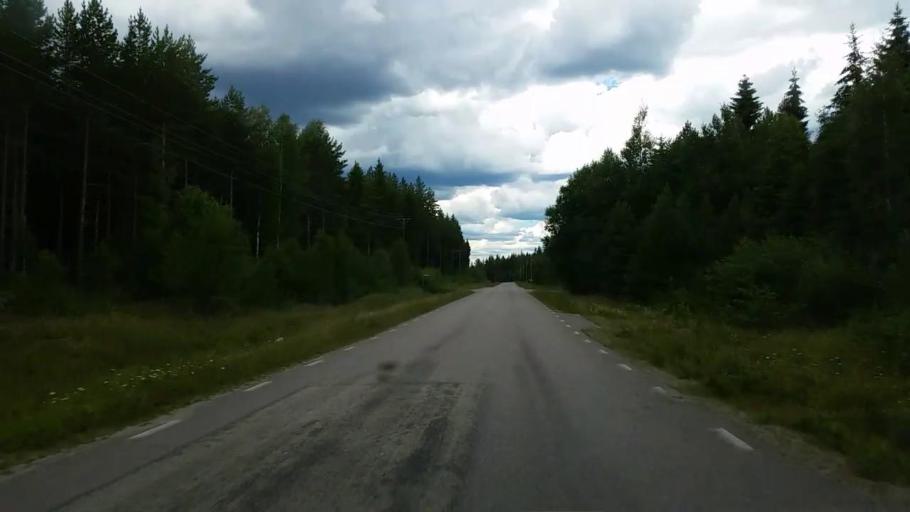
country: SE
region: Gaevleborg
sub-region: Ovanakers Kommun
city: Edsbyn
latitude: 61.4286
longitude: 15.8991
